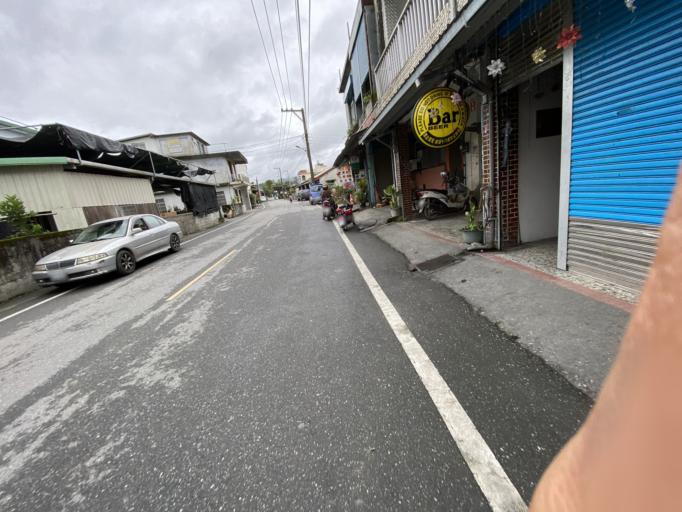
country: TW
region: Taiwan
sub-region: Hualien
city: Hualian
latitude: 23.6578
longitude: 121.4508
